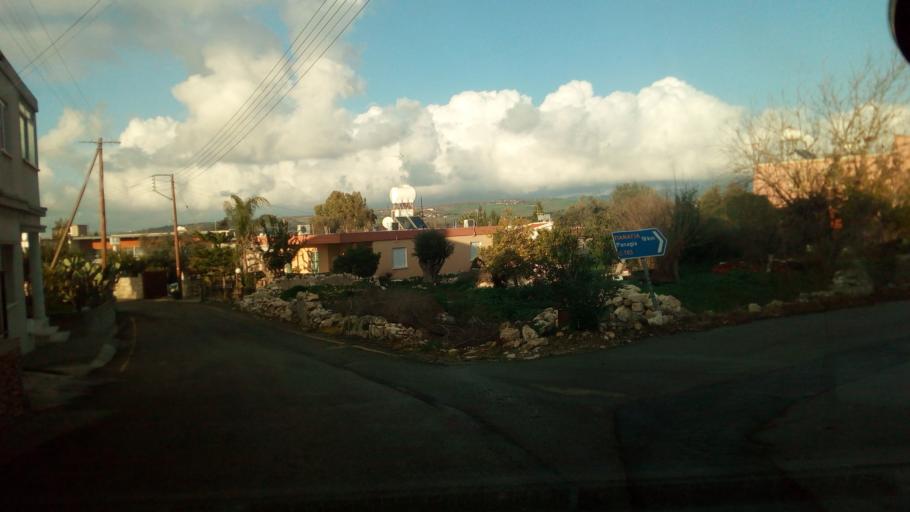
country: CY
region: Pafos
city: Mesogi
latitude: 34.8844
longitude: 32.5080
